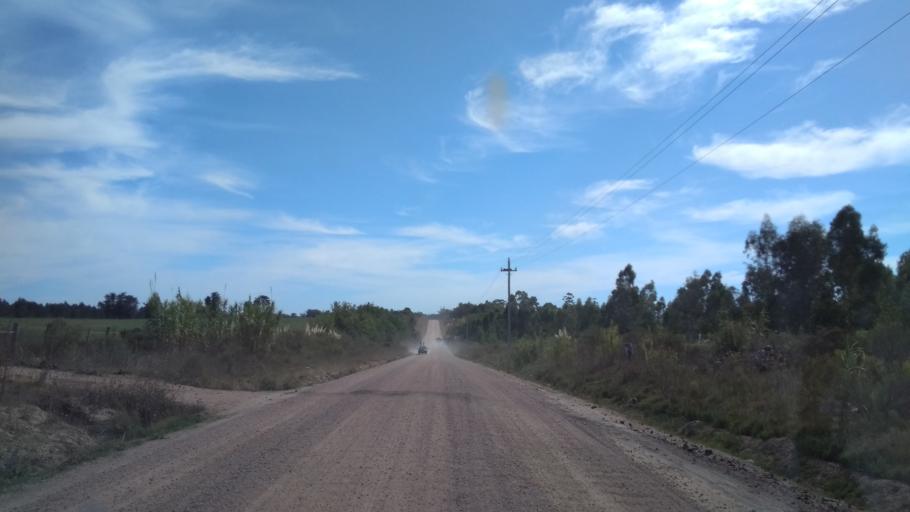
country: UY
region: Canelones
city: Joaquin Suarez
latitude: -34.7166
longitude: -56.0254
